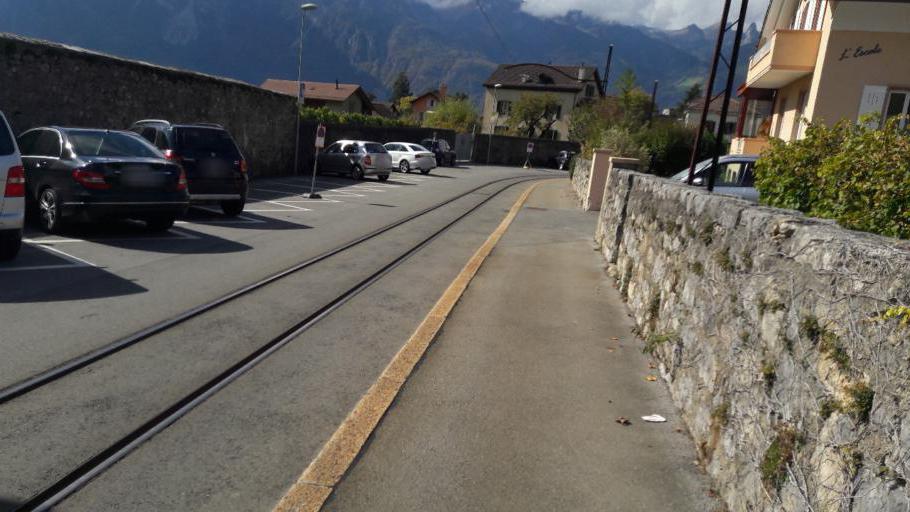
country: CH
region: Vaud
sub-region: Aigle District
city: Aigle
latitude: 46.3165
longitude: 6.9723
